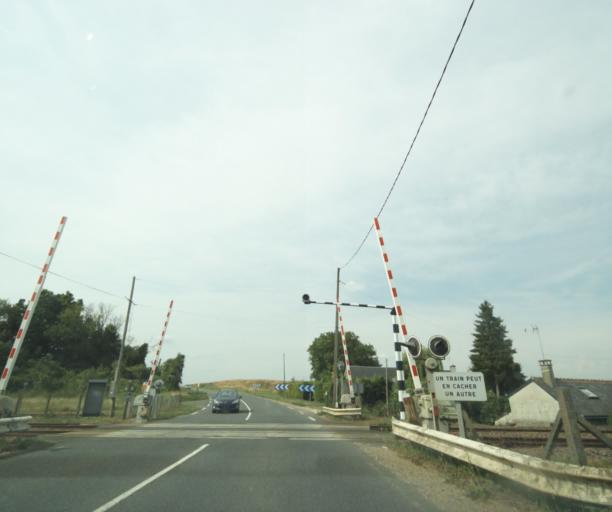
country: FR
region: Centre
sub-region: Departement d'Indre-et-Loire
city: Neuille-Pont-Pierre
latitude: 47.5630
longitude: 0.5499
